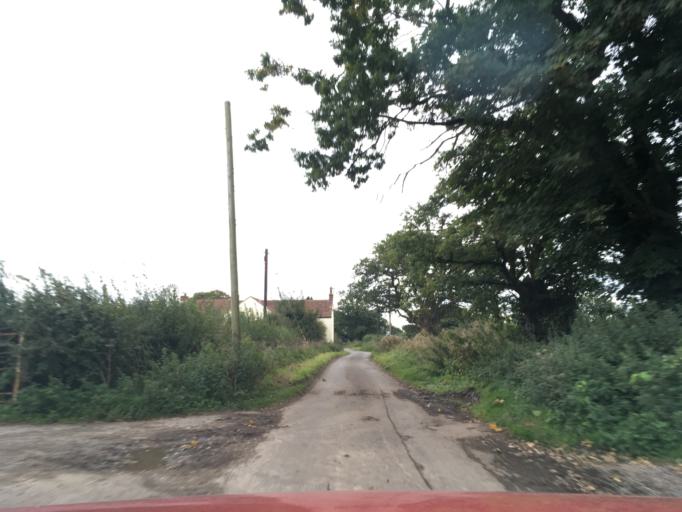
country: GB
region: England
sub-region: South Gloucestershire
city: Yate
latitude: 51.5582
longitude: -2.4462
